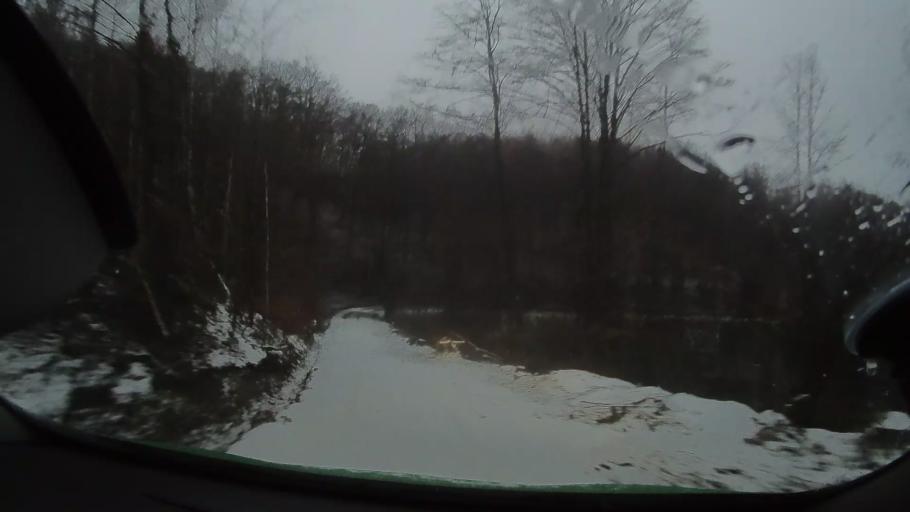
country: RO
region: Alba
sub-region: Comuna Avram Iancu
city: Avram Iancu
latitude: 46.3014
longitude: 22.7934
